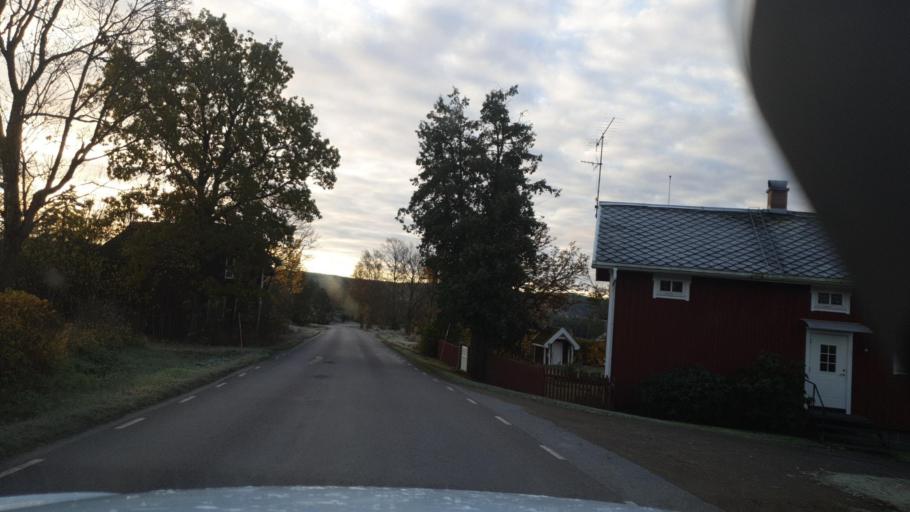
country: SE
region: Vaermland
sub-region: Eda Kommun
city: Charlottenberg
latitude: 59.7462
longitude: 12.1635
